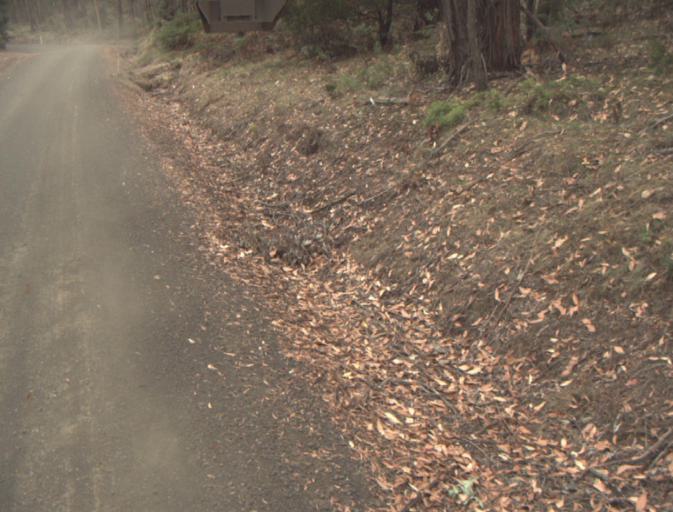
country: AU
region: Tasmania
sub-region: Northern Midlands
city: Evandale
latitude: -41.4932
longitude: 147.5480
